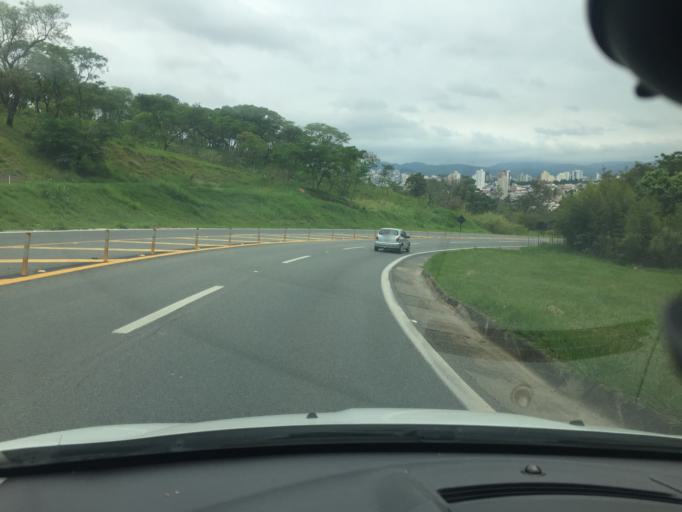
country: BR
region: Sao Paulo
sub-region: Jundiai
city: Jundiai
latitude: -23.1679
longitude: -46.8780
